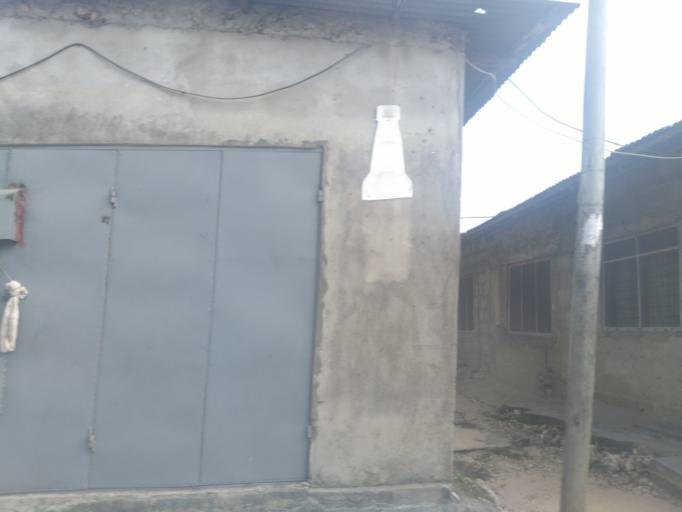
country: TZ
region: Zanzibar Urban/West
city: Zanzibar
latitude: -6.1694
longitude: 39.2046
